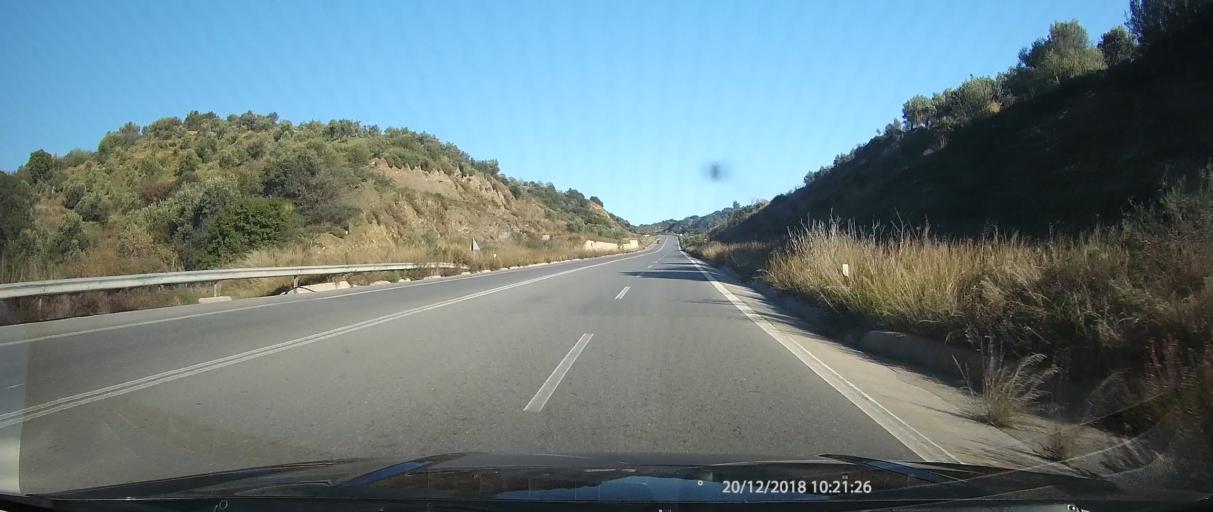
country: GR
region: Peloponnese
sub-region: Nomos Lakonias
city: Magoula
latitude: 37.1595
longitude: 22.4251
